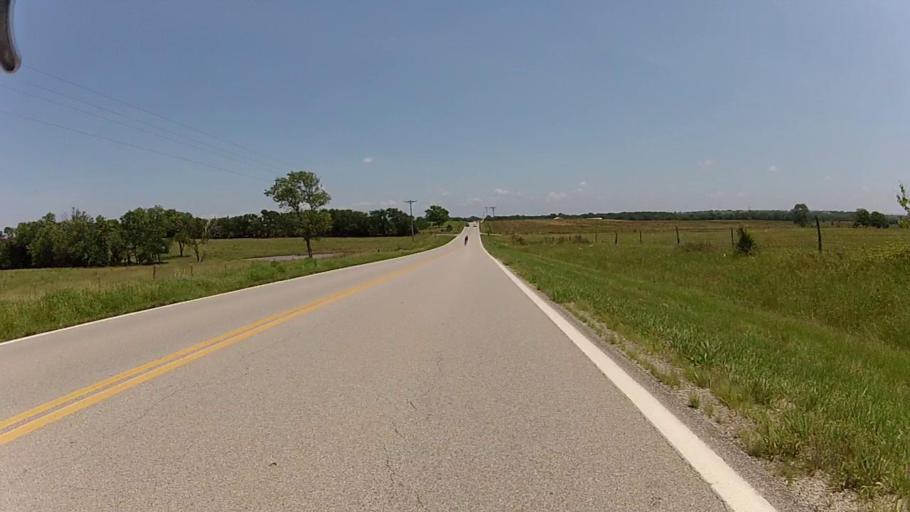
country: US
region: Kansas
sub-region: Montgomery County
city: Cherryvale
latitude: 37.1937
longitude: -95.5231
